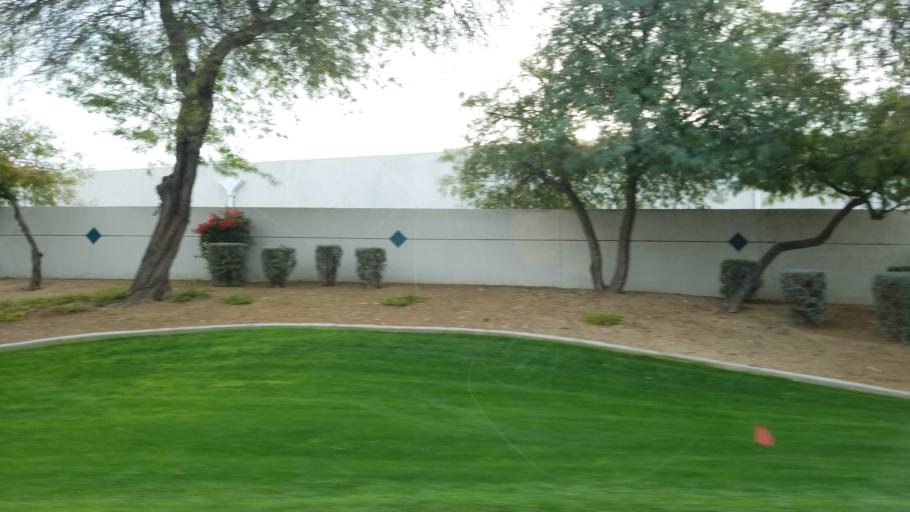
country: US
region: Arizona
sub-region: Maricopa County
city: Paradise Valley
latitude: 33.6042
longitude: -111.9761
